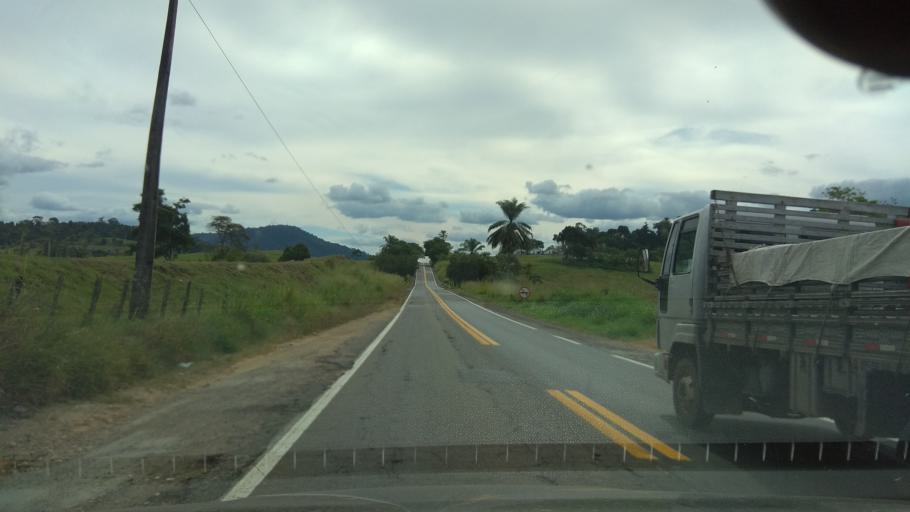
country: BR
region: Bahia
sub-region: Ipiau
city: Ipiau
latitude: -14.1916
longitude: -39.6544
